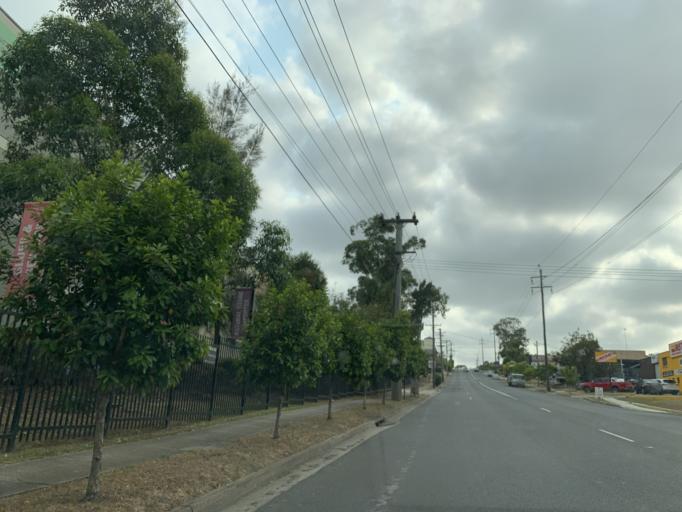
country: AU
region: New South Wales
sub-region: Parramatta
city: Constitution Hill
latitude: -33.7754
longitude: 150.9568
